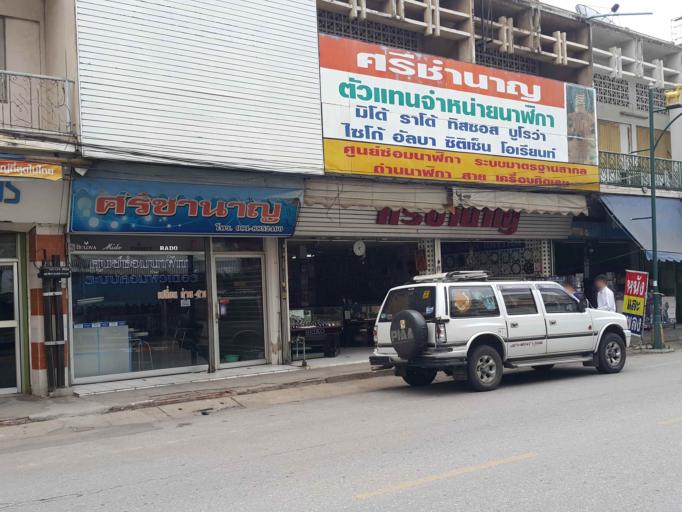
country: TH
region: Lamphun
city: Lamphun
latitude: 18.5762
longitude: 99.0065
